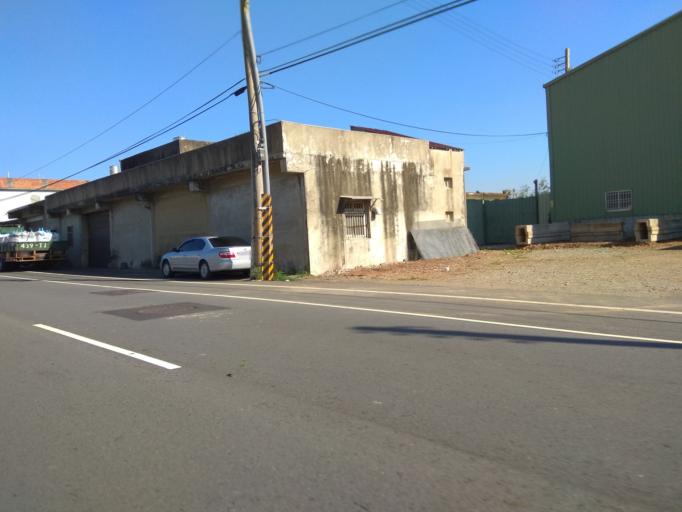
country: TW
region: Taiwan
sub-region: Hsinchu
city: Zhubei
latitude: 25.0281
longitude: 121.0664
